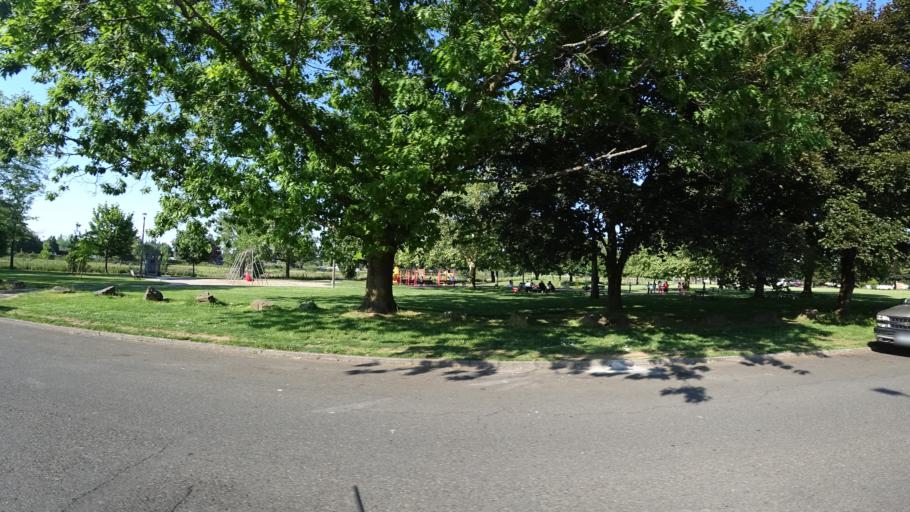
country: US
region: Oregon
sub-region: Multnomah County
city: Lents
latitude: 45.5133
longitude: -122.5058
